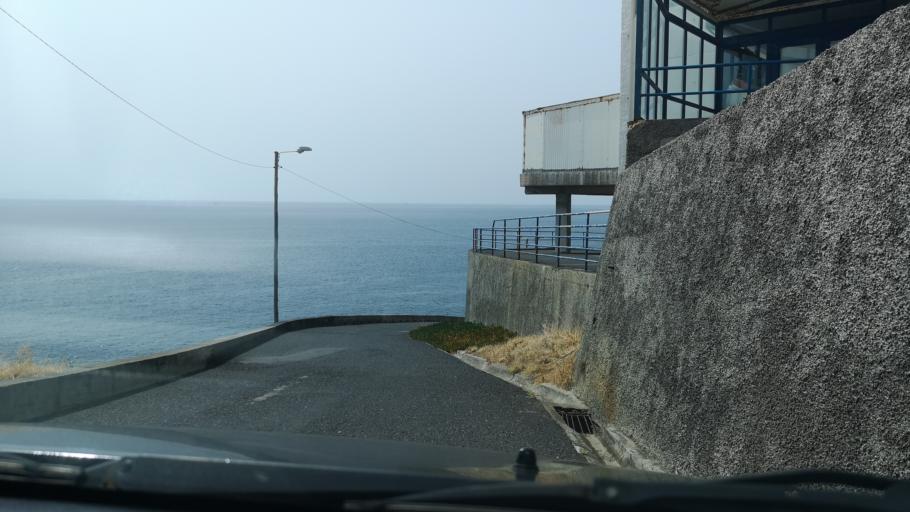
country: PT
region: Madeira
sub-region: Santa Cruz
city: Santa Cruz
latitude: 32.6638
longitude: -16.8037
